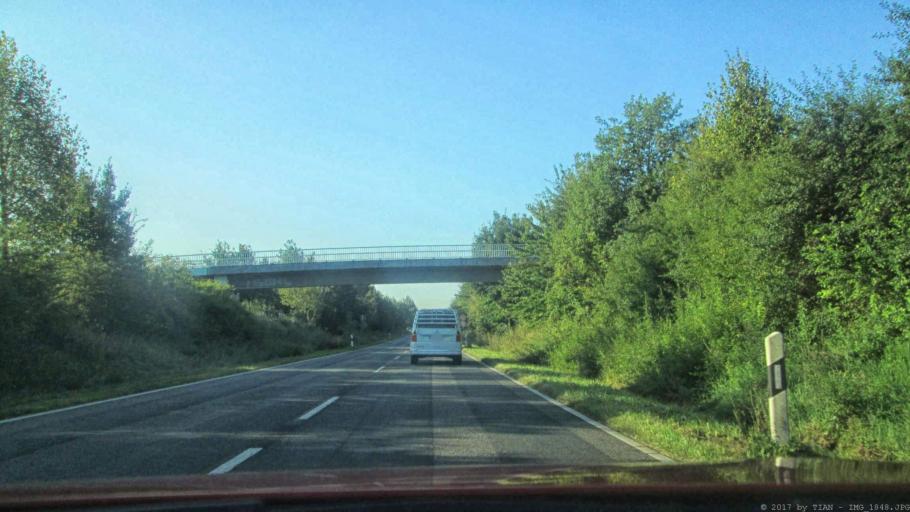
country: DE
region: Lower Saxony
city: Wolfsburg
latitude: 52.4422
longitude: 10.8254
